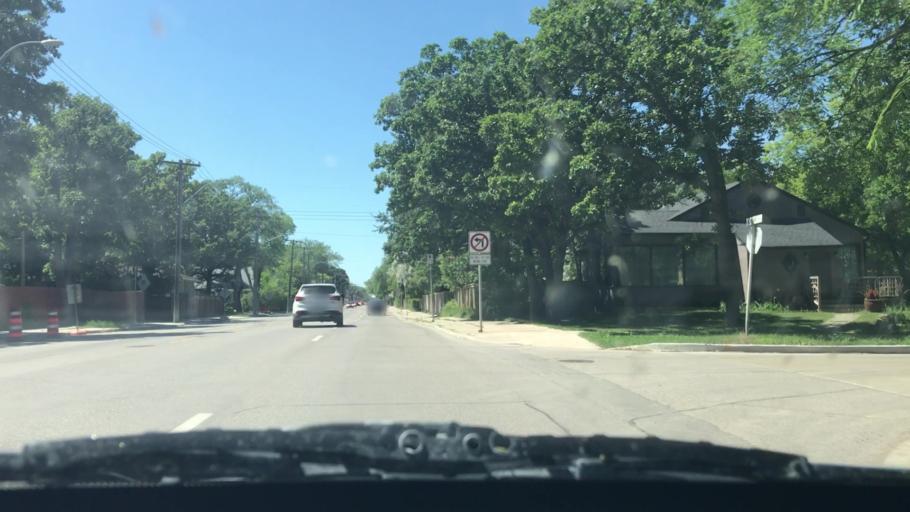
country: CA
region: Manitoba
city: Winnipeg
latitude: 49.8735
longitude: -97.1753
